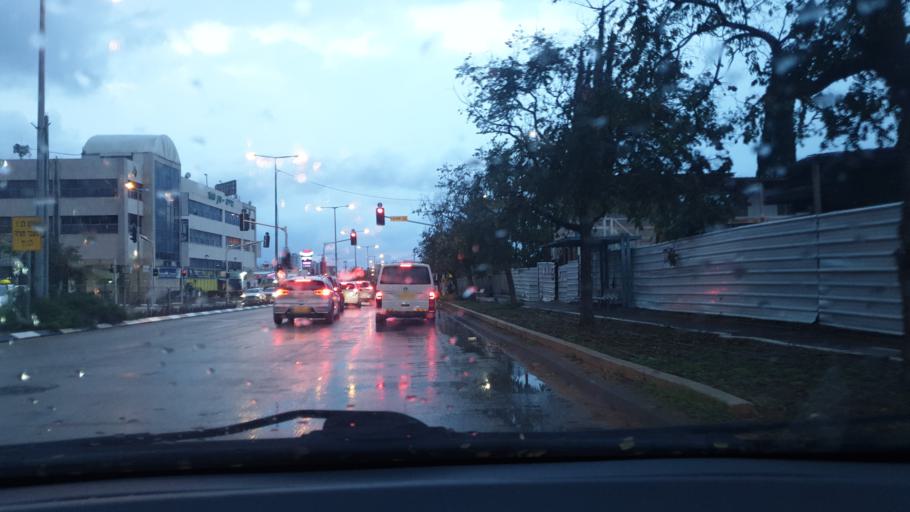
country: IL
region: Central District
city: Bet Dagan
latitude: 31.9750
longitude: 34.8144
